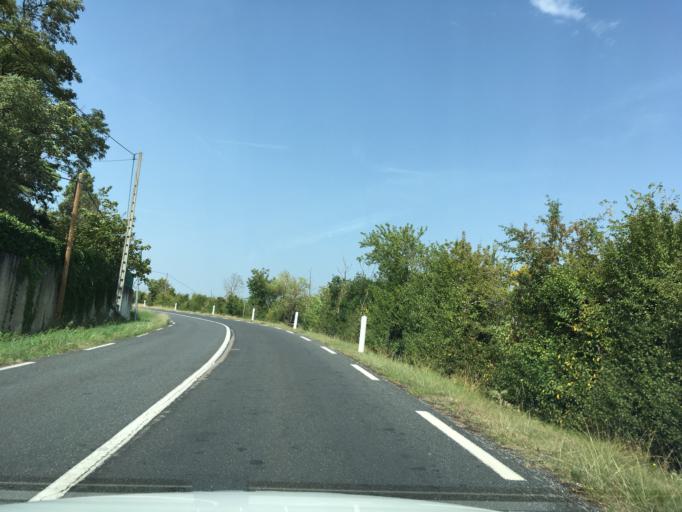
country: FR
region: Midi-Pyrenees
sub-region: Departement du Tarn
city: Castres
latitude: 43.6154
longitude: 2.2187
